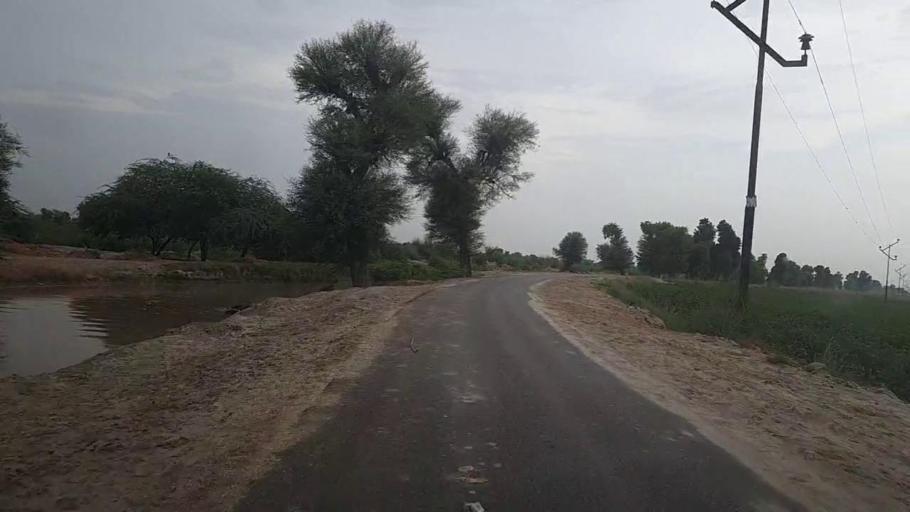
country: PK
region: Sindh
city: Karaundi
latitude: 26.9621
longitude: 68.3658
